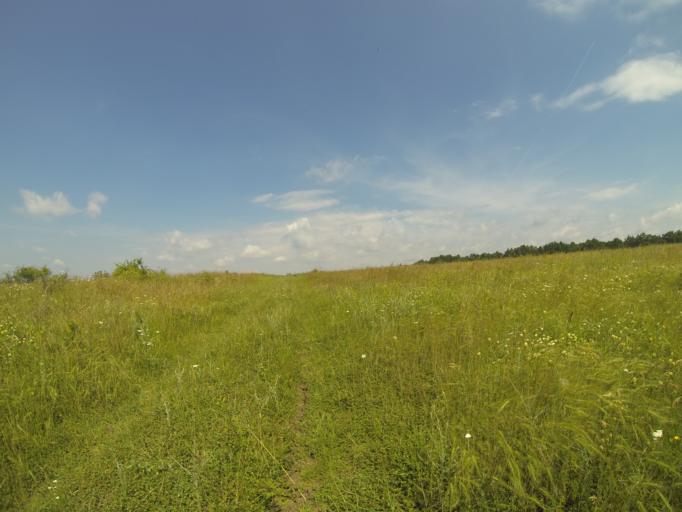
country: RO
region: Gorj
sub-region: Comuna Crusetu
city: Crusetu
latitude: 44.6191
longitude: 23.6227
